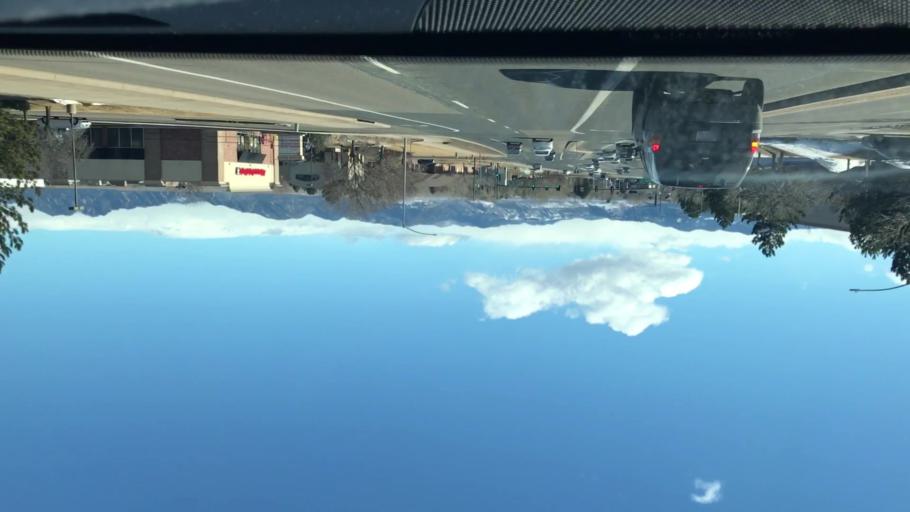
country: US
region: Colorado
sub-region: Adams County
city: Westminster
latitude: 39.8637
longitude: -105.0792
